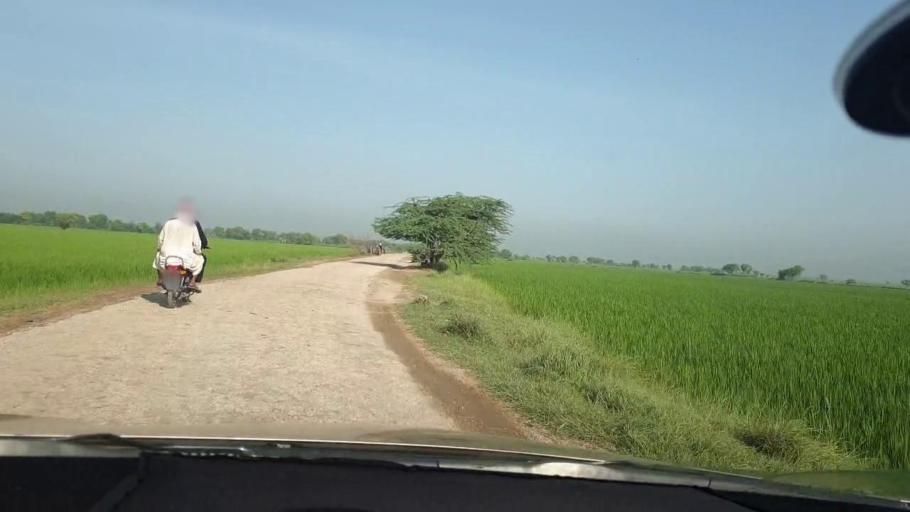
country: PK
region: Sindh
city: Kambar
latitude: 27.6567
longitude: 68.0276
